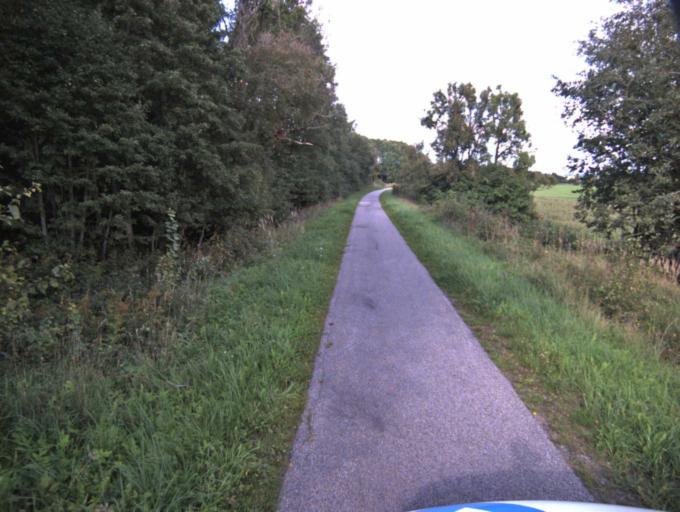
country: SE
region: Vaestra Goetaland
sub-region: Ulricehamns Kommun
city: Ulricehamn
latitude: 57.8915
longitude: 13.4384
